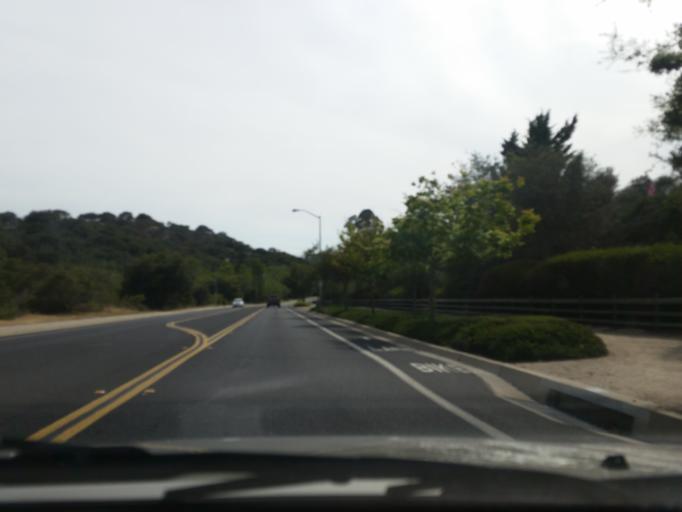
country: US
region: California
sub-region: San Luis Obispo County
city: Arroyo Grande
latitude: 35.1354
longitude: -120.5929
